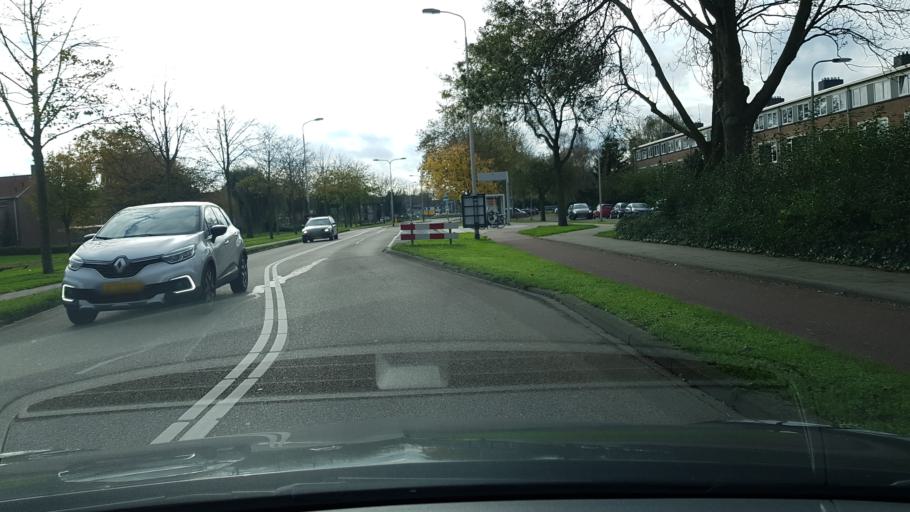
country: NL
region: South Holland
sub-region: Gemeente Hillegom
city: Hillegom
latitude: 52.2919
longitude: 4.5905
